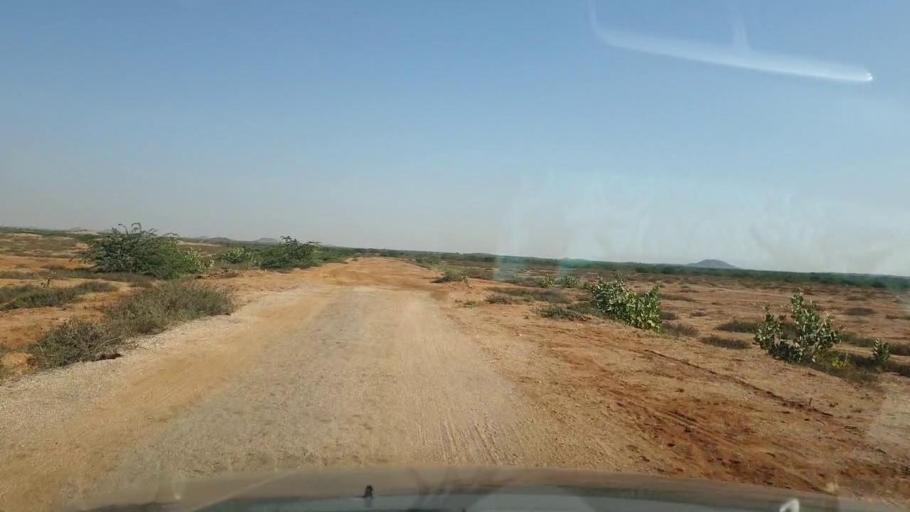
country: PK
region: Sindh
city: Thatta
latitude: 24.8854
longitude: 67.7994
